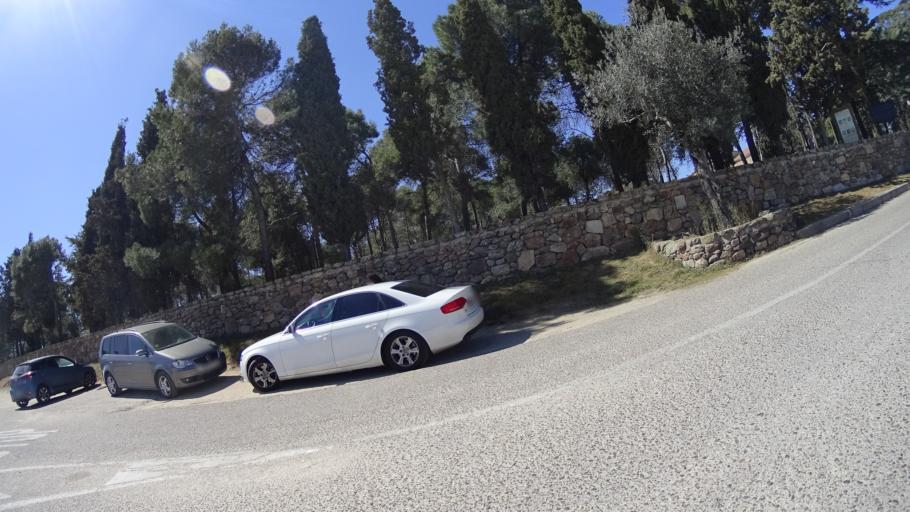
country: ES
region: Madrid
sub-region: Provincia de Madrid
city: Colmenar Viejo
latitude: 40.7028
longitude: -3.7686
